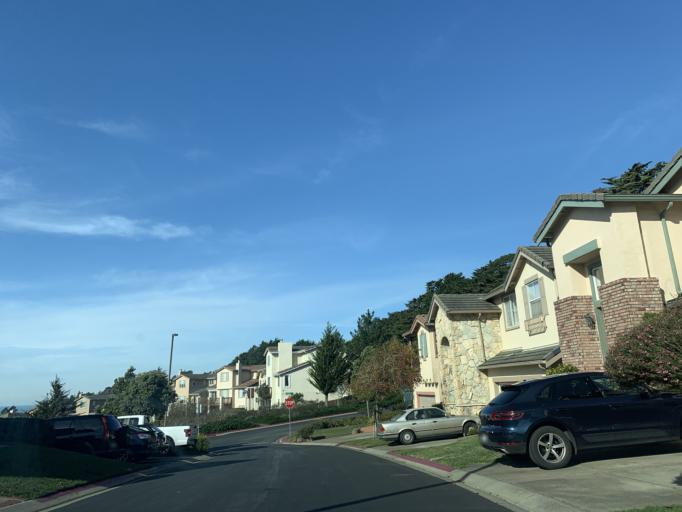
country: US
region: California
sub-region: San Mateo County
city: Pacifica
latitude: 37.6394
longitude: -122.4662
